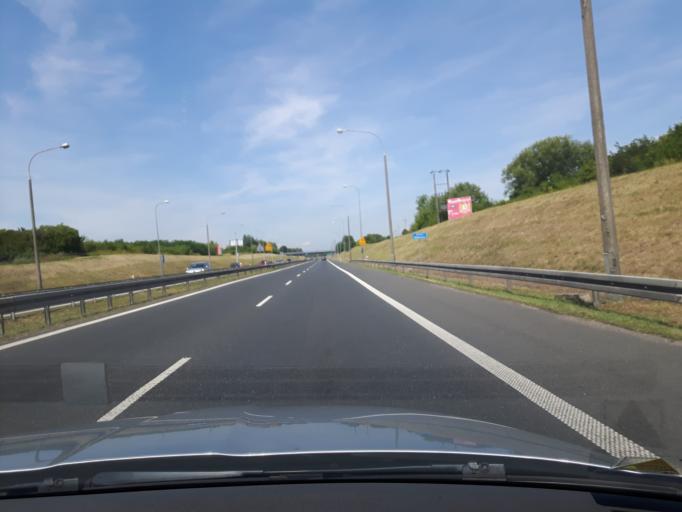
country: PL
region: Masovian Voivodeship
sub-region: Powiat nowodworski
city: Zakroczym
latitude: 52.4298
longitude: 20.6538
